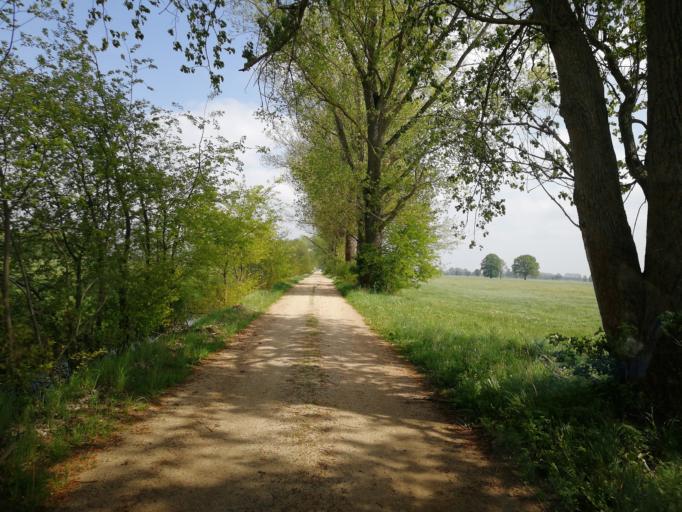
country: DE
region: Brandenburg
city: Doberlug-Kirchhain
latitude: 51.6753
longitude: 13.5382
